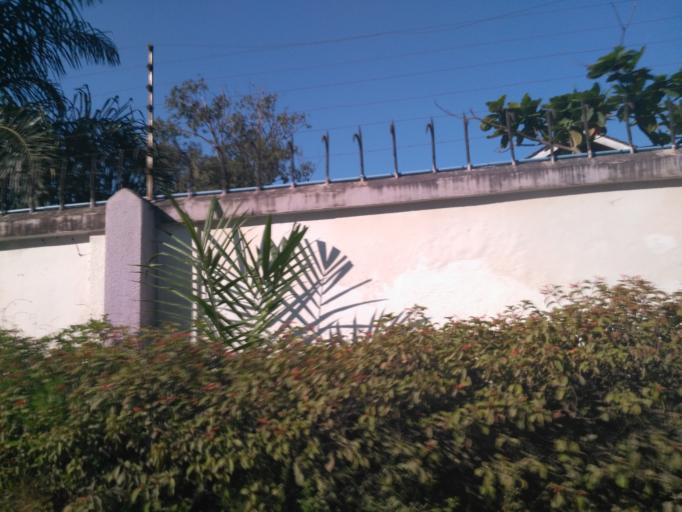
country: TZ
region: Dar es Salaam
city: Magomeni
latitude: -6.7623
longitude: 39.2518
